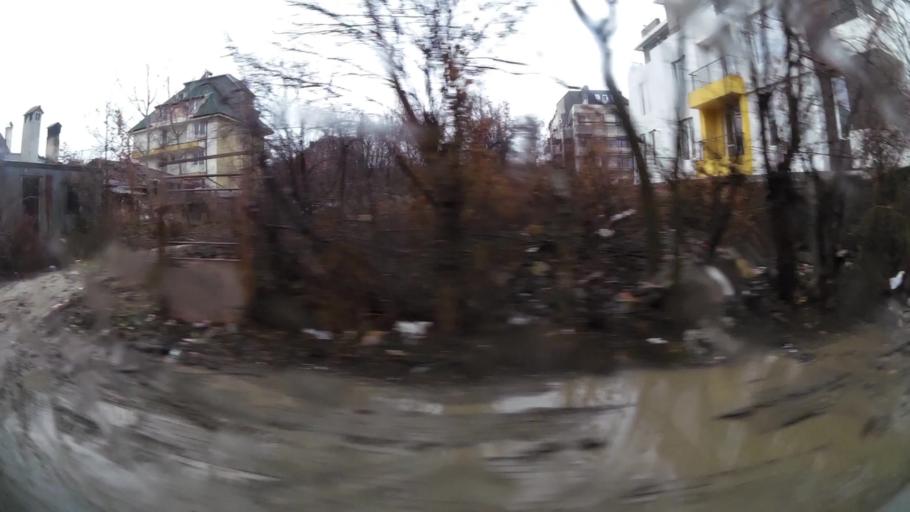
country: BG
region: Sofia-Capital
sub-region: Stolichna Obshtina
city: Sofia
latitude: 42.6533
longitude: 23.3203
